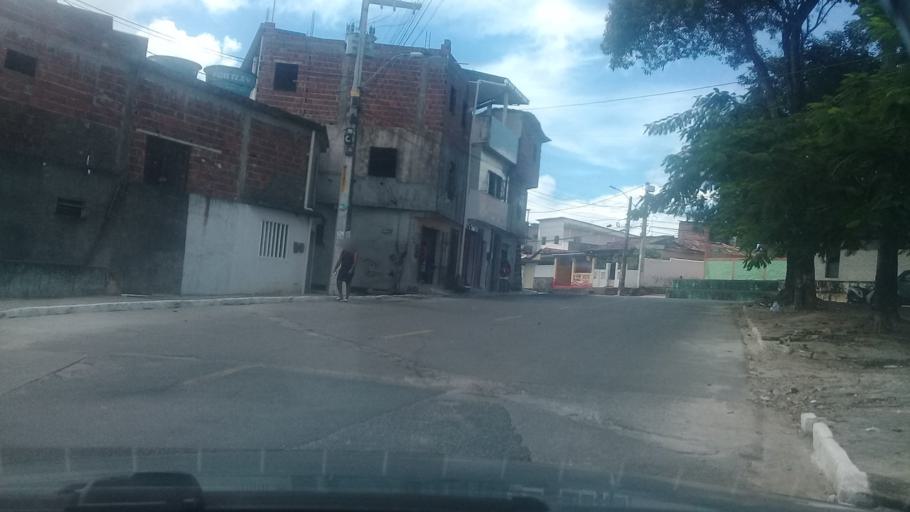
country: BR
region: Pernambuco
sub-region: Jaboatao Dos Guararapes
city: Jaboatao dos Guararapes
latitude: -8.1222
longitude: -34.9473
